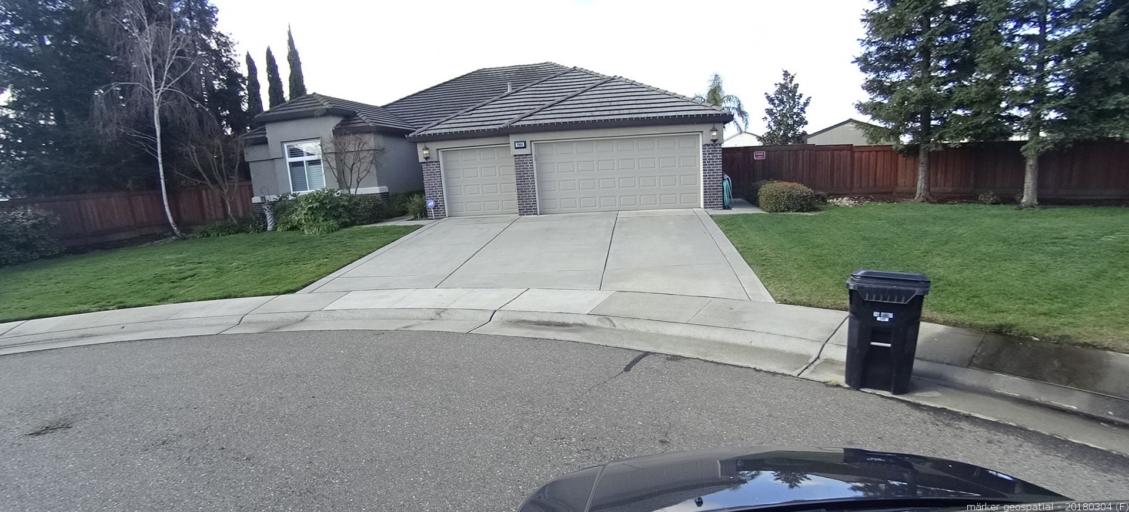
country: US
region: California
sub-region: Sacramento County
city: Vineyard
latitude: 38.4610
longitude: -121.3250
